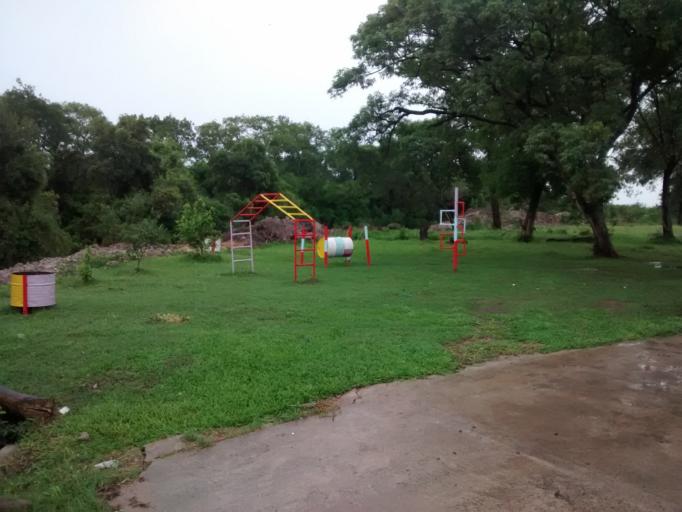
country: AR
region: Chaco
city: Fontana
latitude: -27.4046
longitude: -58.9887
